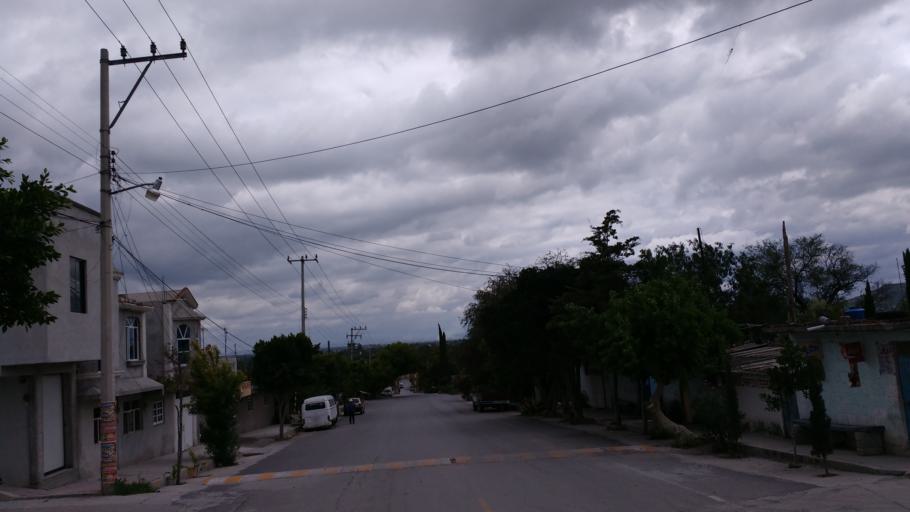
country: MX
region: Hidalgo
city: Mixquiahuala de Juarez
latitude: 20.2490
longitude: -99.2441
